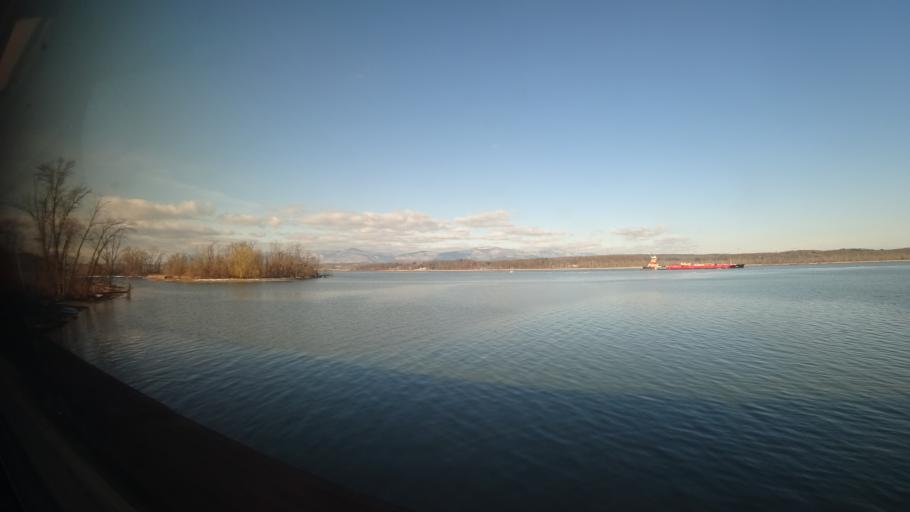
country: US
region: New York
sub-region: Greene County
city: Catskill
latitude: 42.1803
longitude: -73.8594
